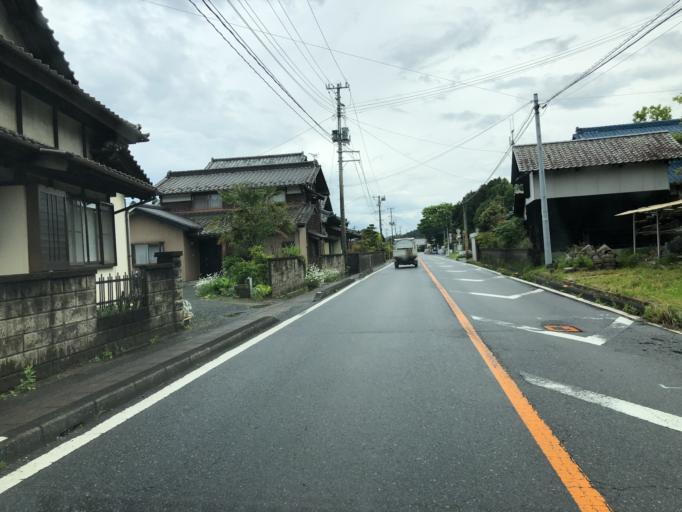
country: JP
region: Fukushima
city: Iwaki
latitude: 36.9508
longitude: 140.7682
